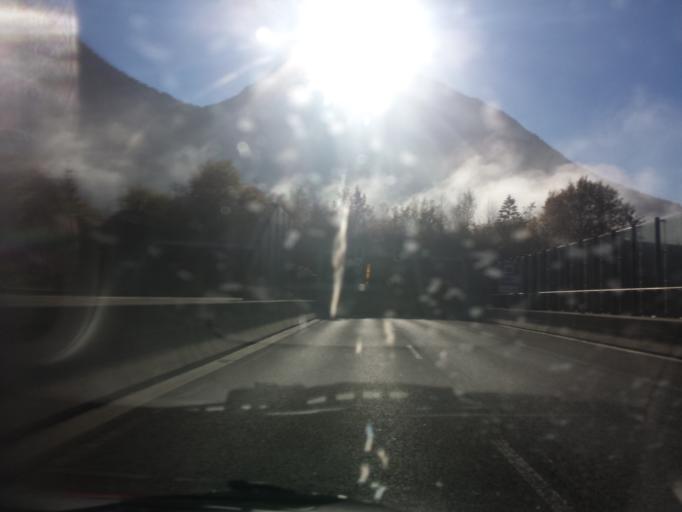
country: DE
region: Bavaria
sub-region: Upper Bavaria
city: Farchant
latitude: 47.5345
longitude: 11.1196
